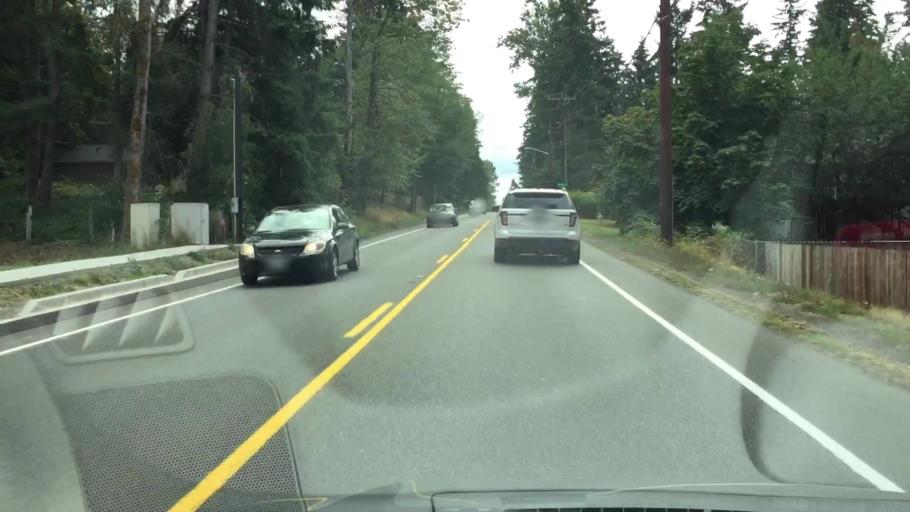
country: US
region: Washington
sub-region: Pierce County
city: South Hill
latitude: 47.1231
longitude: -122.2666
